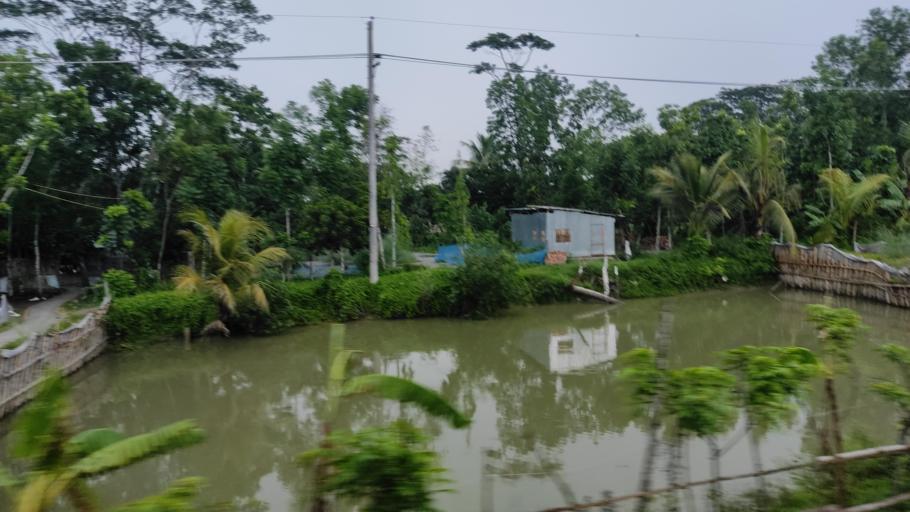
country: BD
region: Barisal
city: Bhandaria
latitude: 22.3186
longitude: 90.3258
